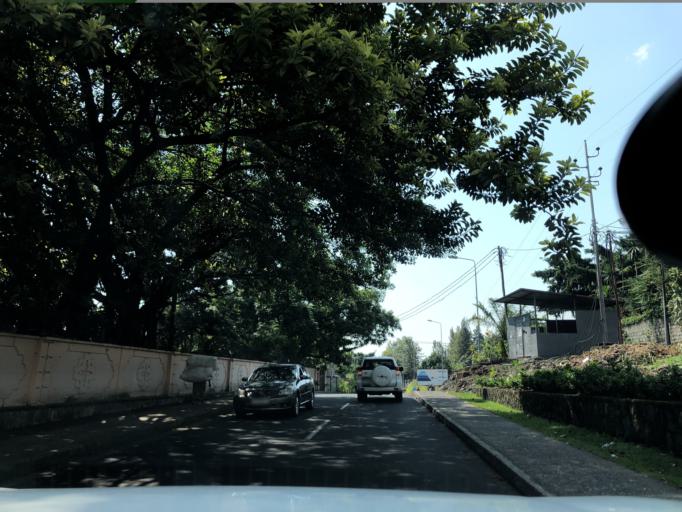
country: CD
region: Nord Kivu
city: Goma
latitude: -1.6750
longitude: 29.2051
